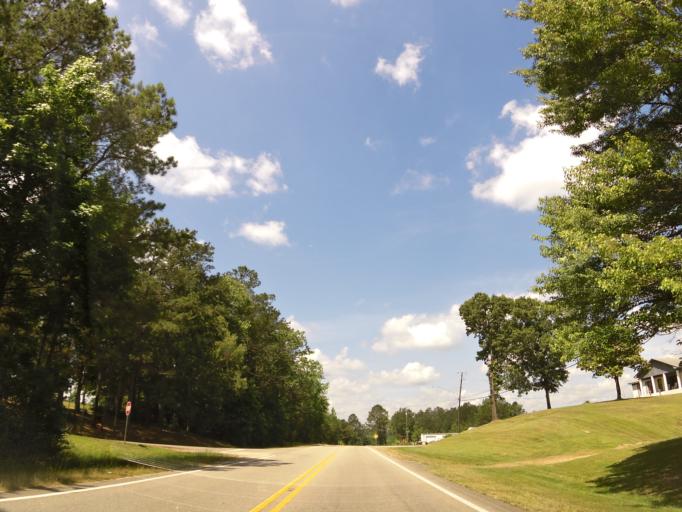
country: US
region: Alabama
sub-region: Marion County
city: Guin
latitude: 33.9569
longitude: -87.9219
